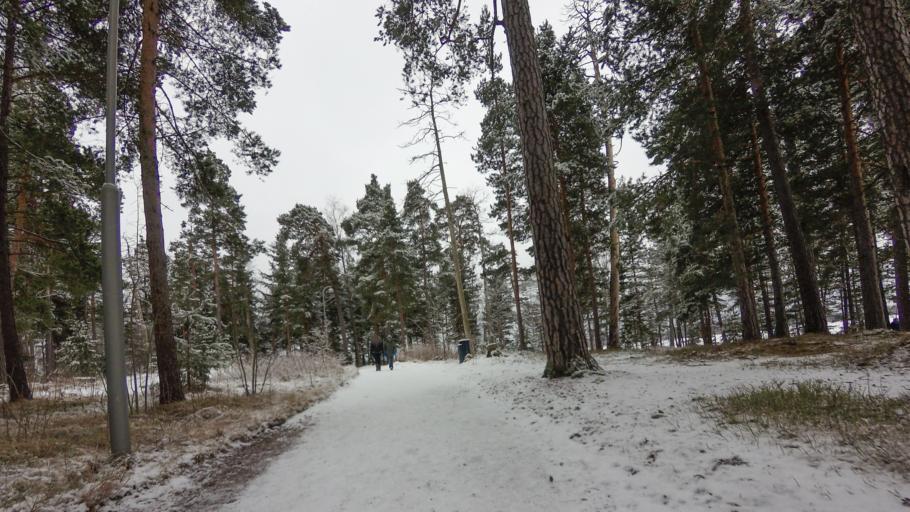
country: FI
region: Uusimaa
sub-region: Helsinki
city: Teekkarikylae
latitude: 60.1782
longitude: 24.8808
